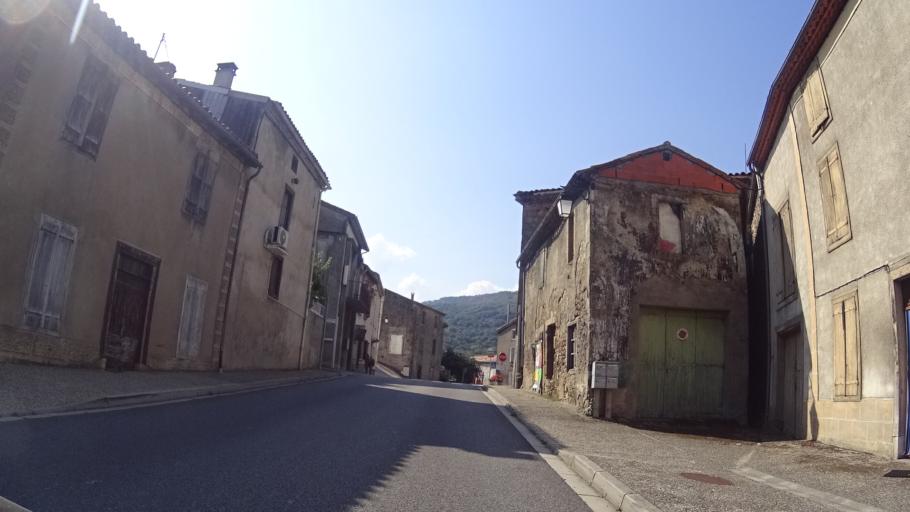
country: FR
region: Midi-Pyrenees
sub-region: Departement de l'Ariege
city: Lavelanet
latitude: 42.9175
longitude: 1.7578
